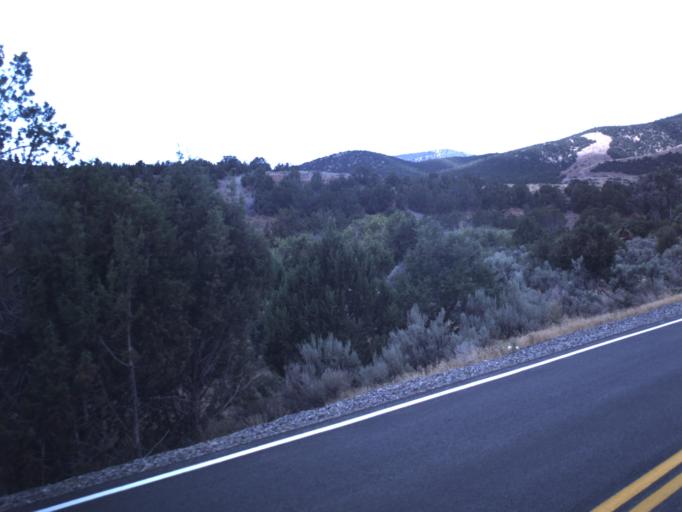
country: US
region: Utah
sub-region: Tooele County
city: Grantsville
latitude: 40.3332
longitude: -112.5217
